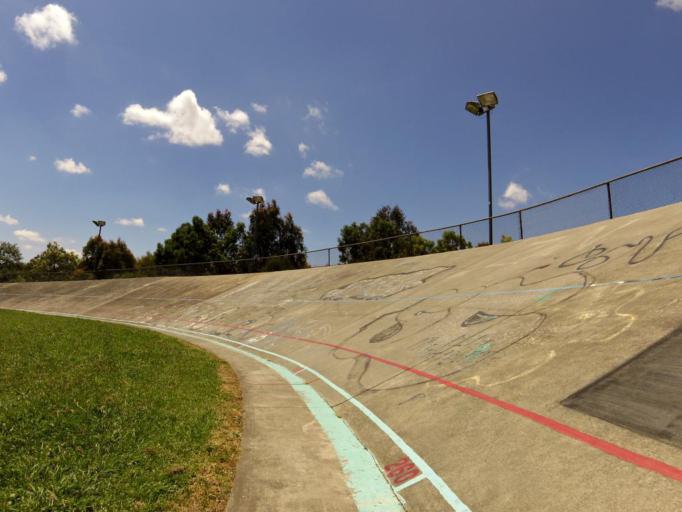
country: AU
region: Victoria
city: Brunswick East
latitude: -37.7615
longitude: 144.9823
